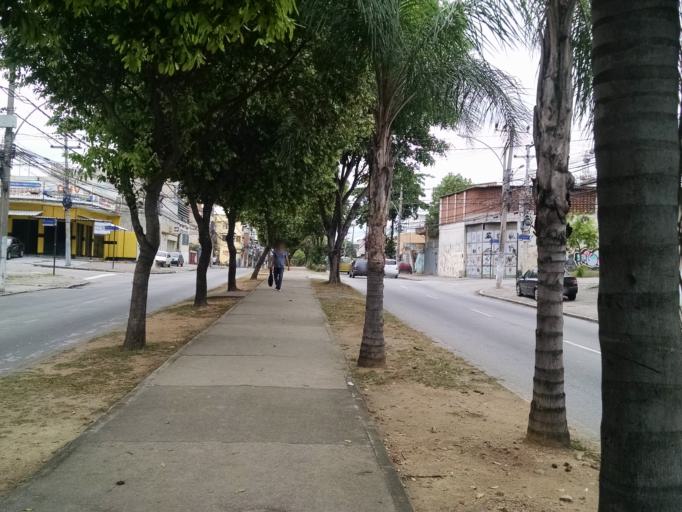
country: BR
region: Rio de Janeiro
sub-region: Duque De Caxias
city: Duque de Caxias
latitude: -22.8278
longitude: -43.3106
